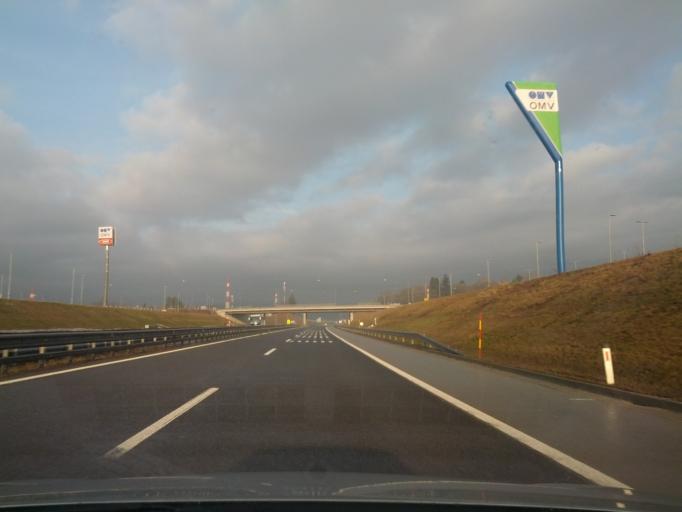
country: SI
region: Radovljica
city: Radovljica
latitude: 46.3385
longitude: 14.1922
